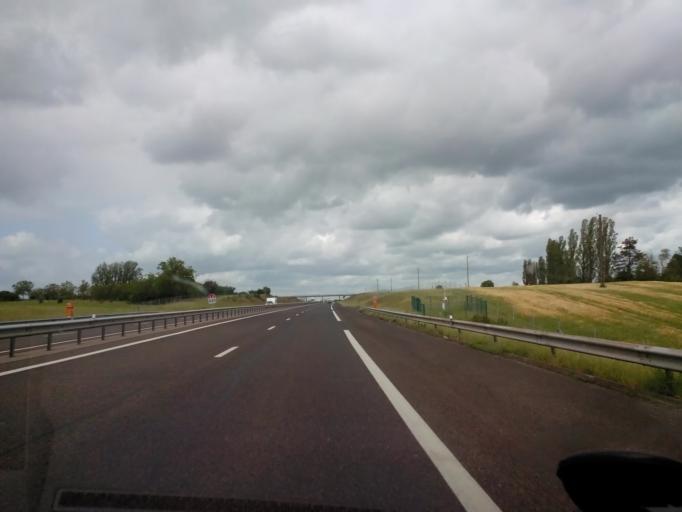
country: FR
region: Lorraine
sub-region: Departement de Meurthe-et-Moselle
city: Blenod-les-Toul
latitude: 48.5800
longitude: 5.8867
